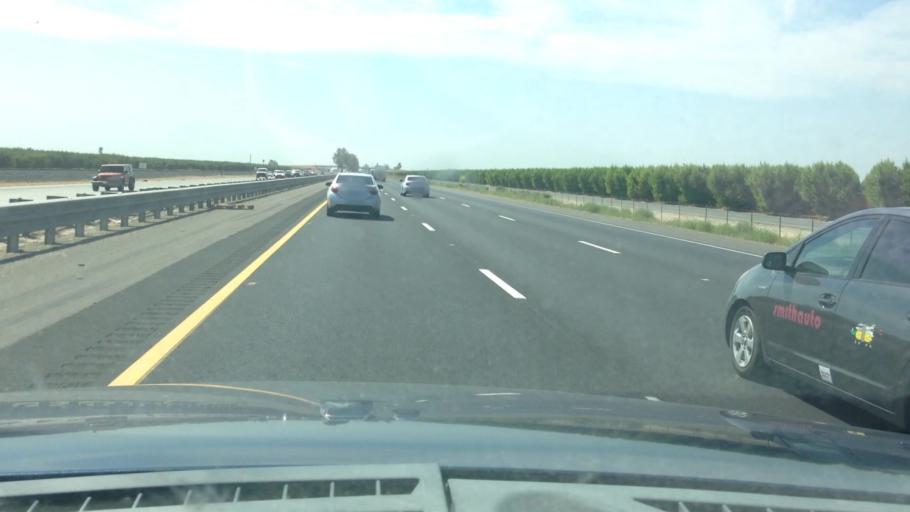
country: US
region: California
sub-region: Tulare County
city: Goshen
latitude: 36.3978
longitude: -119.4521
